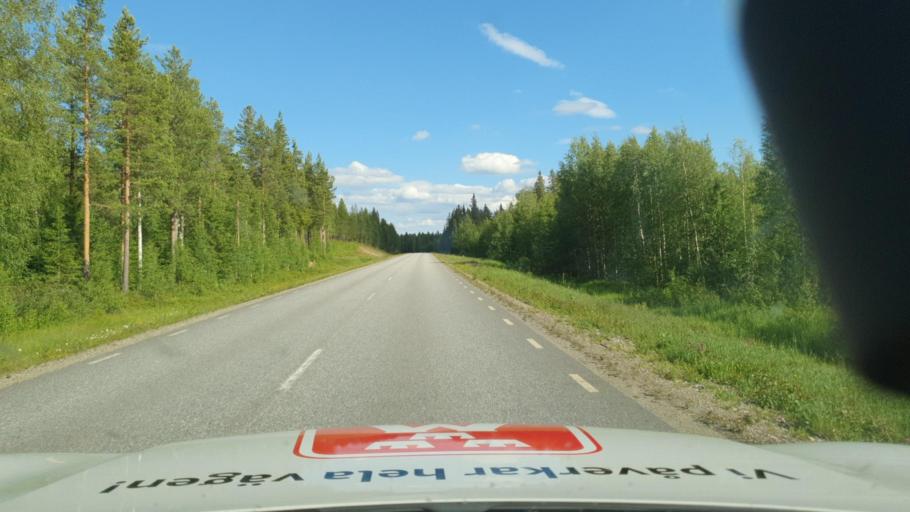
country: SE
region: Vaesterbotten
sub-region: Skelleftea Kommun
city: Langsele
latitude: 64.8212
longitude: 19.9379
